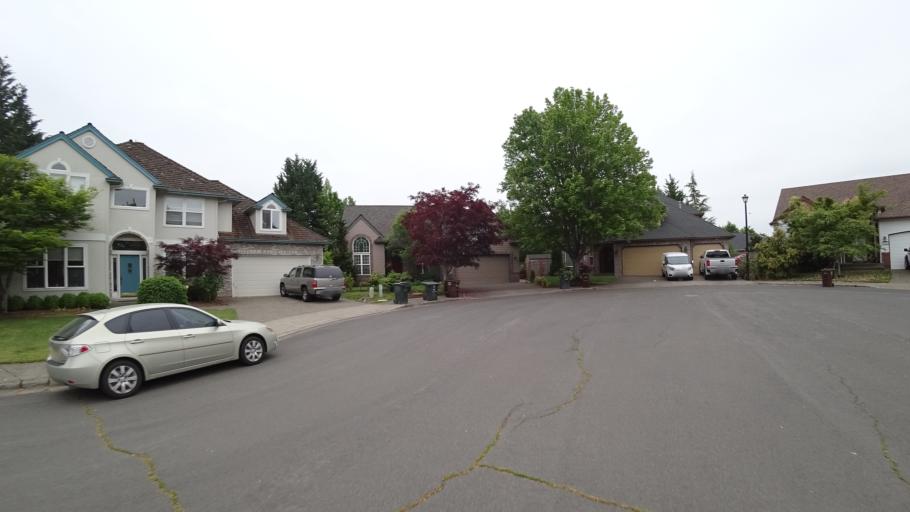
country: US
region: Oregon
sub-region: Washington County
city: Bethany
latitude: 45.5466
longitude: -122.8602
